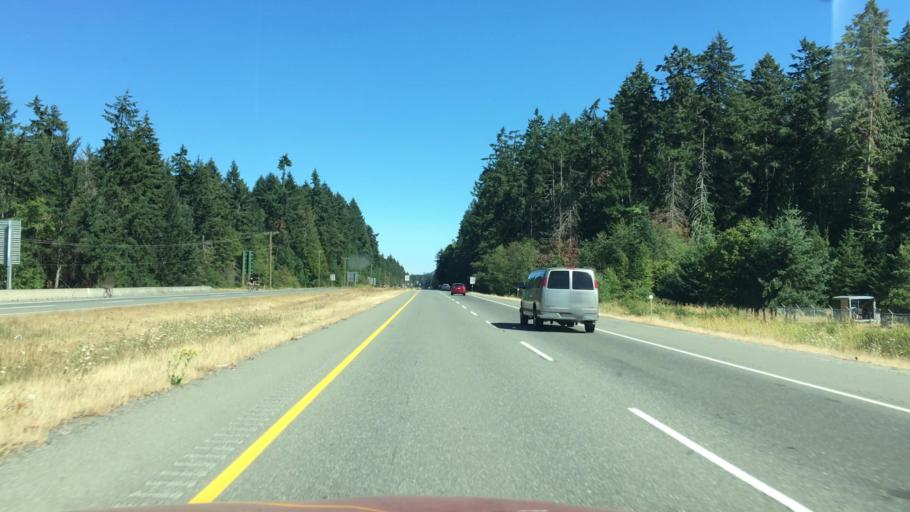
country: CA
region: British Columbia
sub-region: Regional District of Nanaimo
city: Parksville
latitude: 49.3036
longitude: -124.3116
